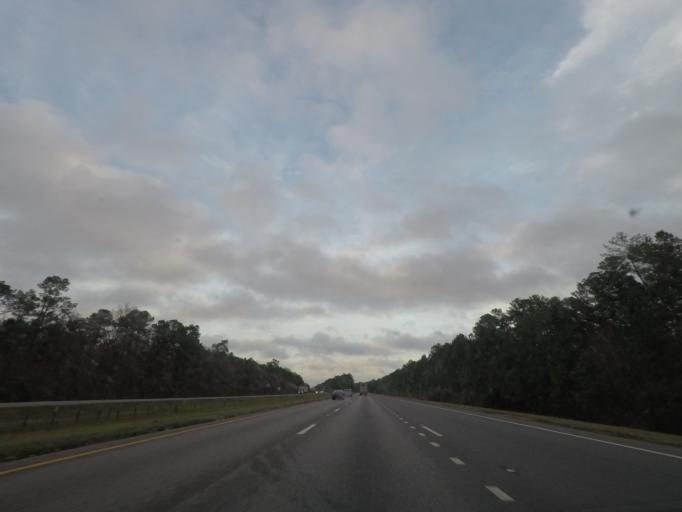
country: US
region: South Carolina
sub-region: Orangeburg County
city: Holly Hill
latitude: 33.3238
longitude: -80.5439
